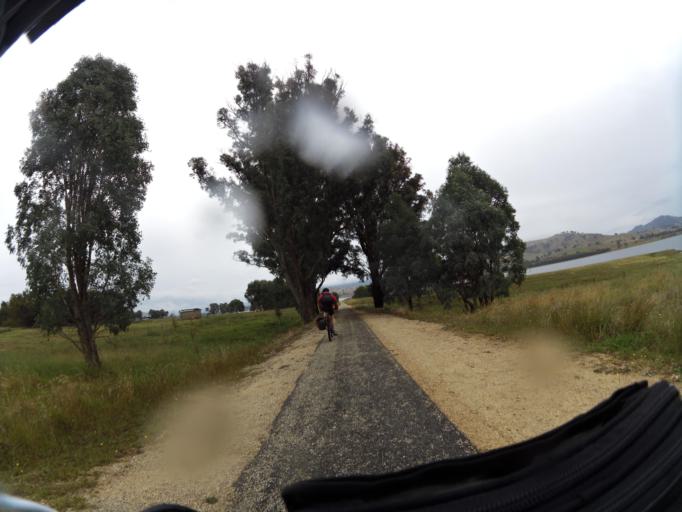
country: AU
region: New South Wales
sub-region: Albury Municipality
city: East Albury
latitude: -36.2326
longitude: 147.0973
